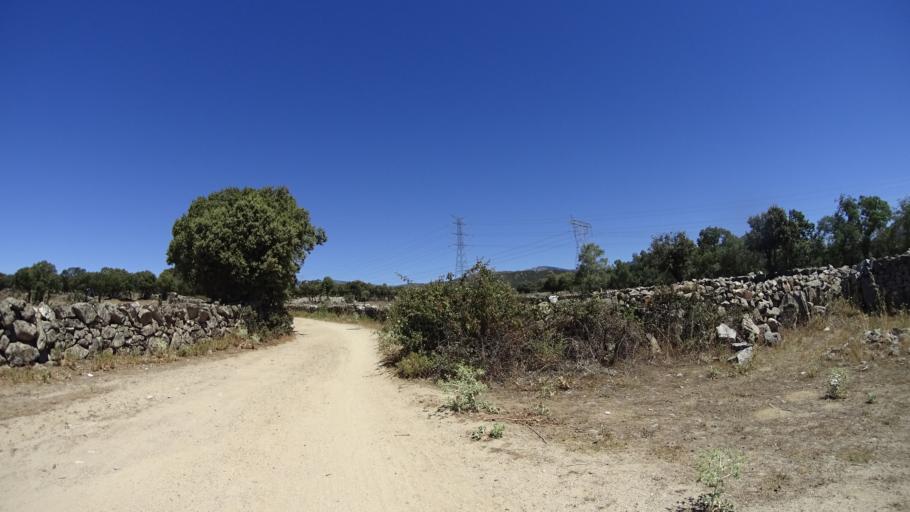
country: ES
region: Madrid
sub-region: Provincia de Madrid
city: Collado Mediano
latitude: 40.6774
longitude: -4.0392
